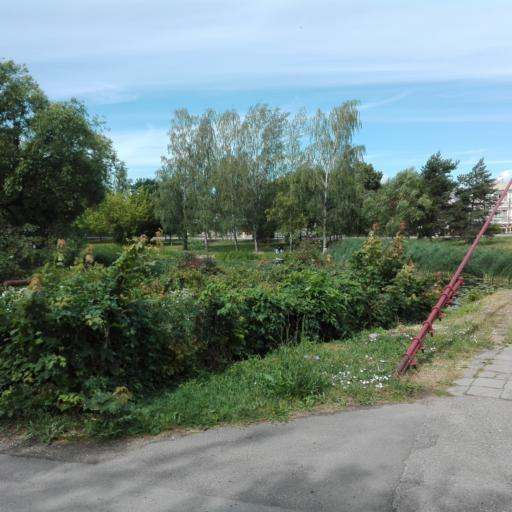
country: LT
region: Panevezys
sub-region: Birzai
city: Birzai
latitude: 56.2021
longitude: 24.7636
